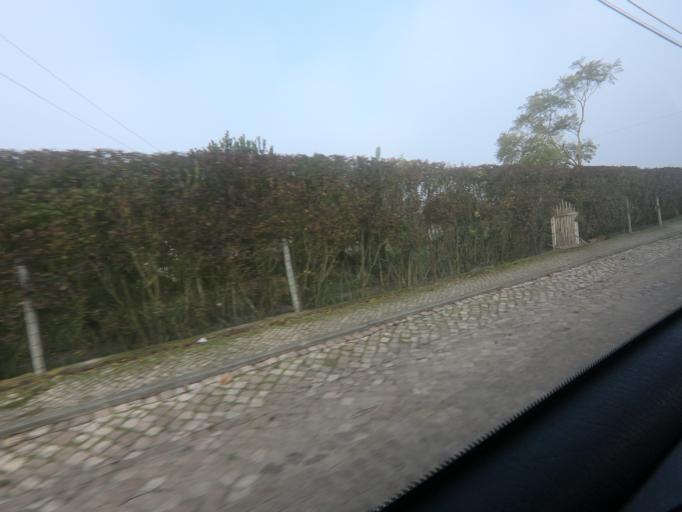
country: PT
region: Setubal
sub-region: Palmela
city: Palmela
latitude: 38.6020
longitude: -8.8976
